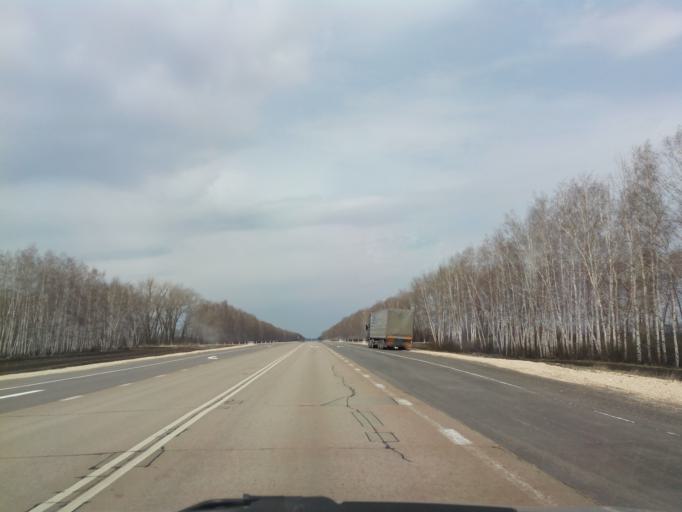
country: RU
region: Tambov
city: Satinka
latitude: 52.2042
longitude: 41.5681
